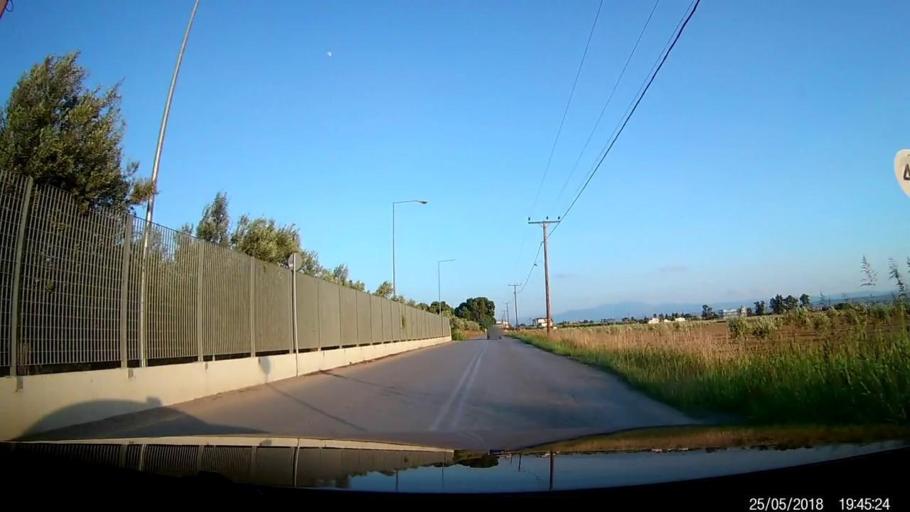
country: GR
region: Central Greece
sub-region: Nomos Evvoias
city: Ayios Nikolaos
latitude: 38.4335
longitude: 23.6329
